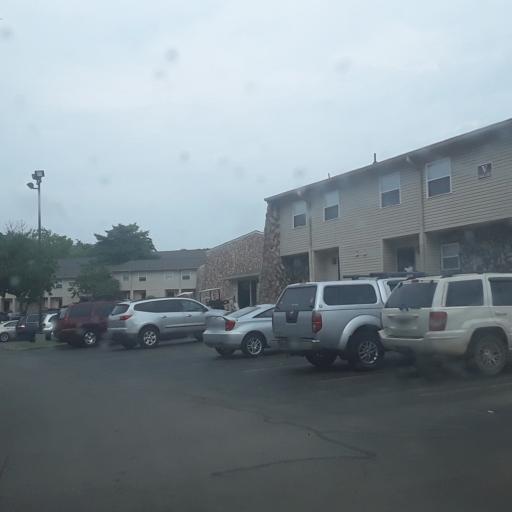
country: US
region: Tennessee
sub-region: Williamson County
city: Brentwood Estates
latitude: 36.0477
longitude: -86.7171
